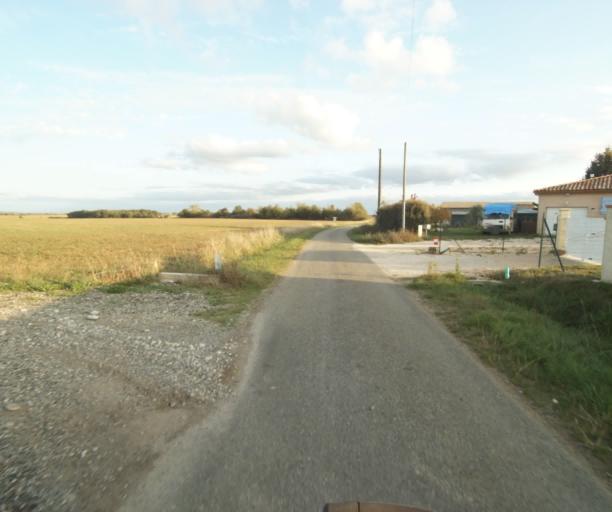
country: FR
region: Midi-Pyrenees
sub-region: Departement du Tarn-et-Garonne
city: Verdun-sur-Garonne
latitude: 43.8224
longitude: 1.1586
